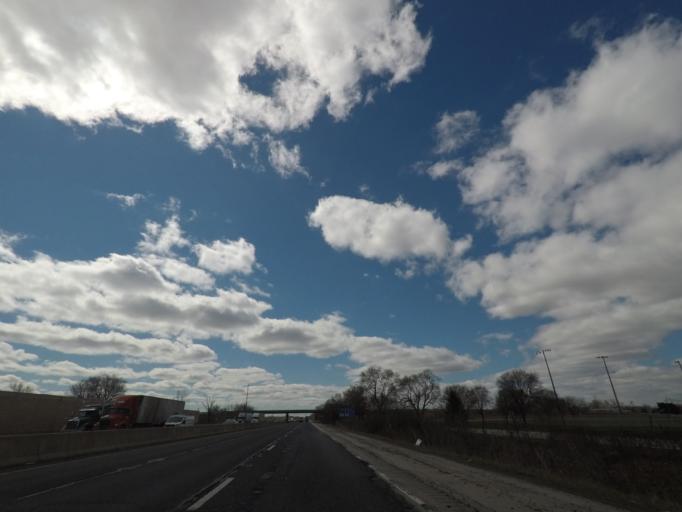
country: US
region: Illinois
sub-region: Will County
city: Crystal Lawns
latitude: 41.6111
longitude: -88.1635
